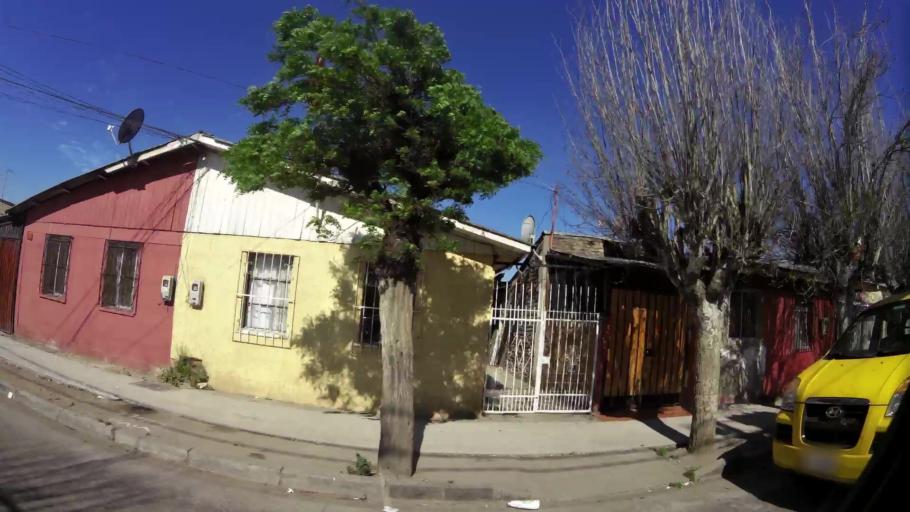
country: CL
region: Santiago Metropolitan
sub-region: Provincia de Santiago
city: Lo Prado
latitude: -33.5140
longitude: -70.6978
